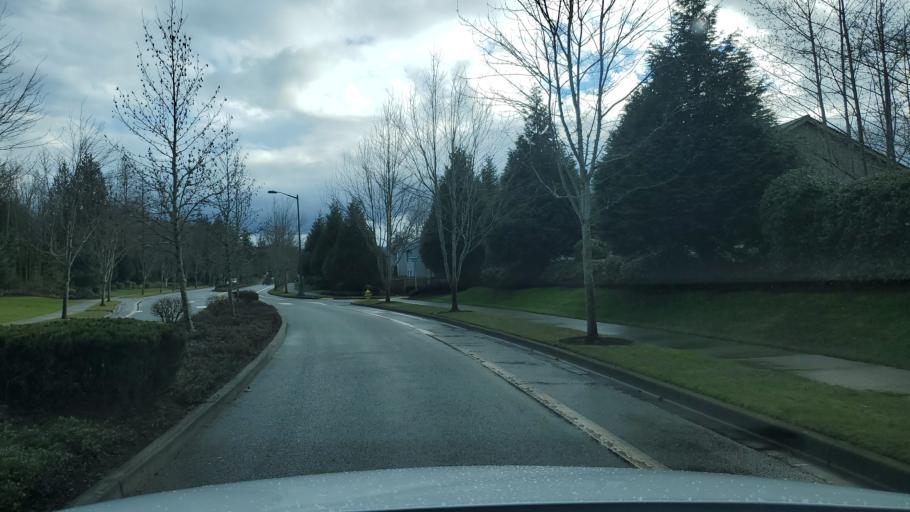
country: US
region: Washington
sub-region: Skagit County
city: Big Lake
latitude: 48.4238
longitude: -122.2784
